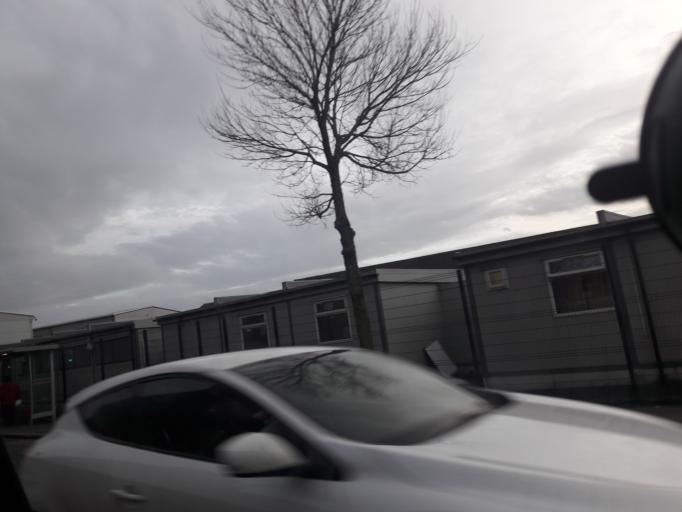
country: GB
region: Northern Ireland
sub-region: City of Belfast
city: Belfast
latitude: 54.6084
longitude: -5.9405
